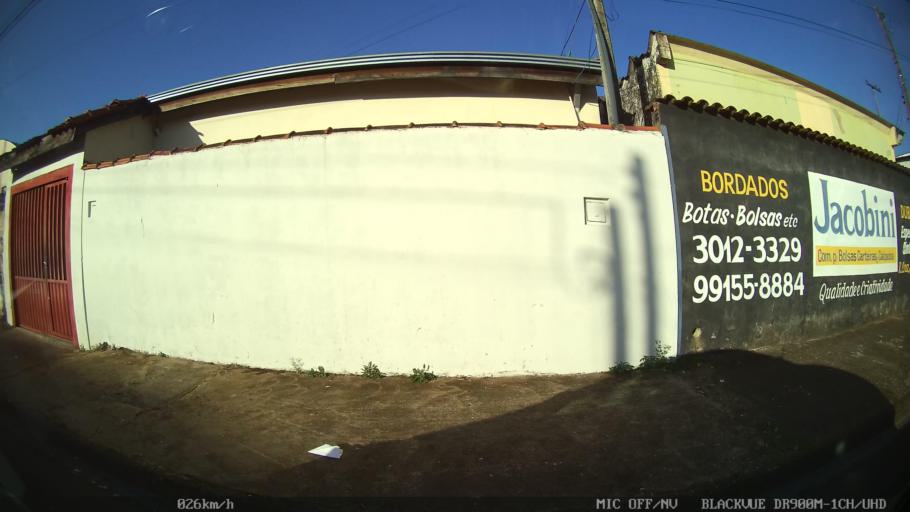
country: BR
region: Sao Paulo
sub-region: Franca
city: Franca
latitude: -20.5252
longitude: -47.3779
